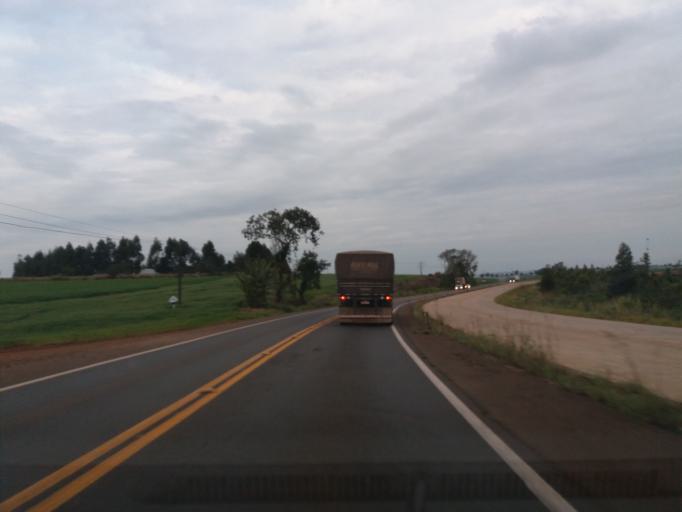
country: BR
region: Parana
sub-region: Cascavel
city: Cascavel
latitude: -25.2422
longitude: -53.5828
